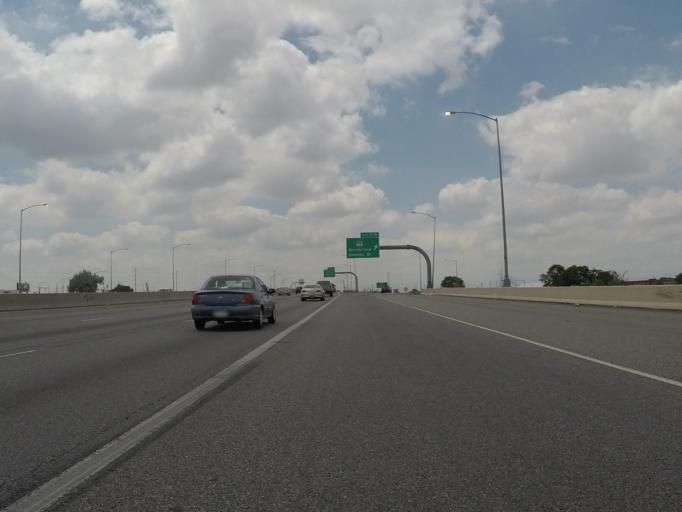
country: US
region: Colorado
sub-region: Adams County
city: Commerce City
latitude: 39.7785
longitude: -104.8998
